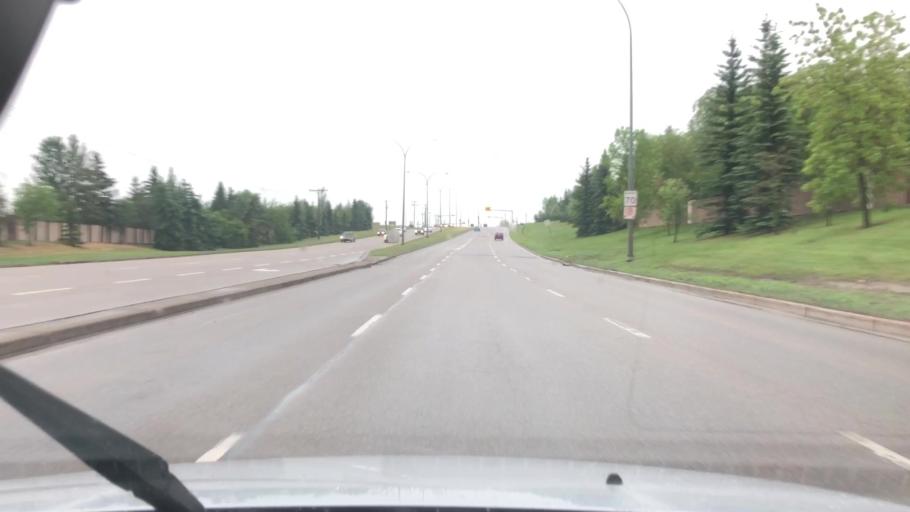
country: CA
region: Alberta
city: Sherwood Park
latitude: 53.5412
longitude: -113.2542
